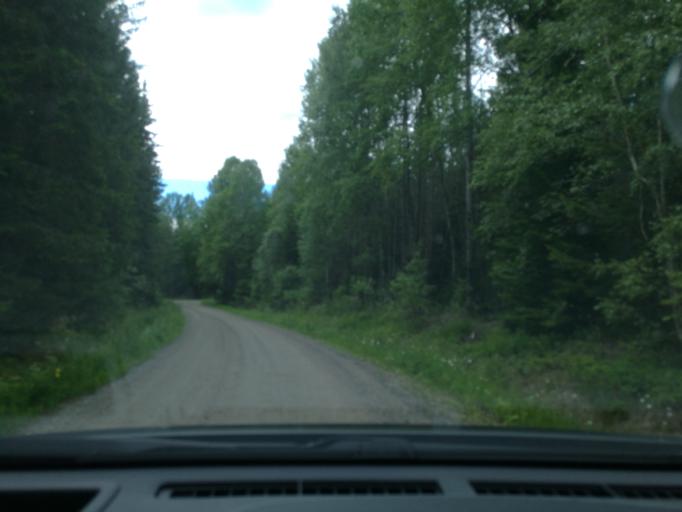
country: SE
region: Vaestmanland
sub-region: Surahammars Kommun
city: Ramnas
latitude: 59.8131
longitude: 16.3141
